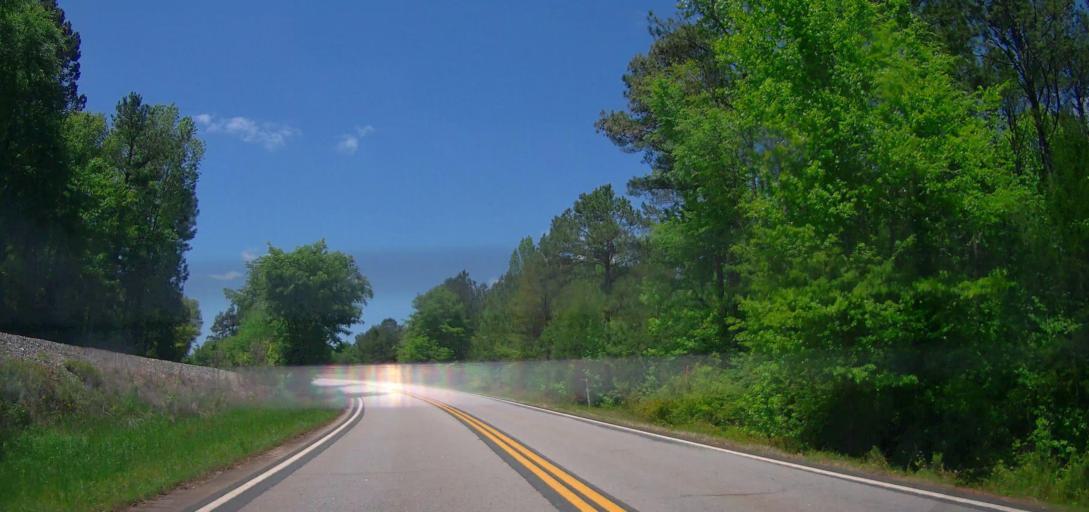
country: US
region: Georgia
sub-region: Jasper County
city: Monticello
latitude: 33.1747
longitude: -83.6443
